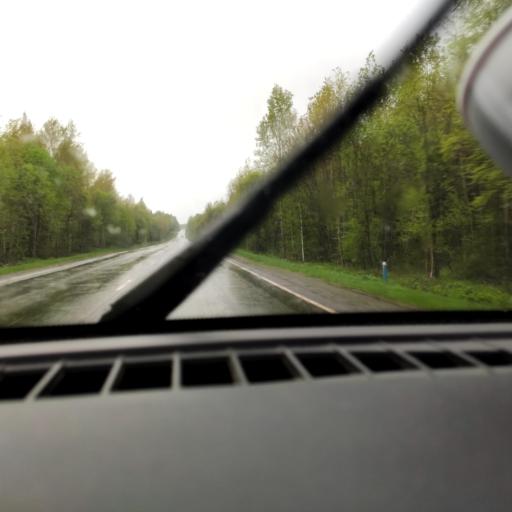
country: RU
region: Perm
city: Polazna
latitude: 58.2732
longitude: 56.1666
